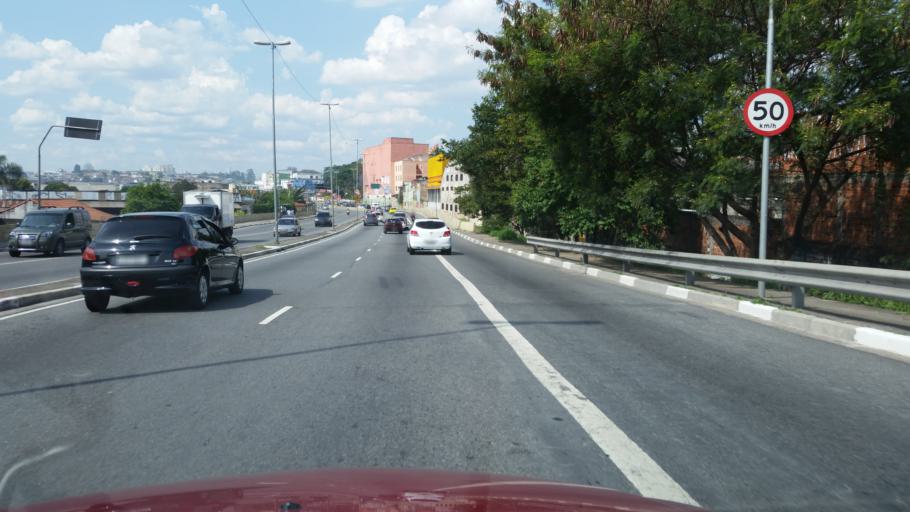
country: BR
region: Sao Paulo
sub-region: Ferraz De Vasconcelos
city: Ferraz de Vasconcelos
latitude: -23.5396
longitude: -46.4583
